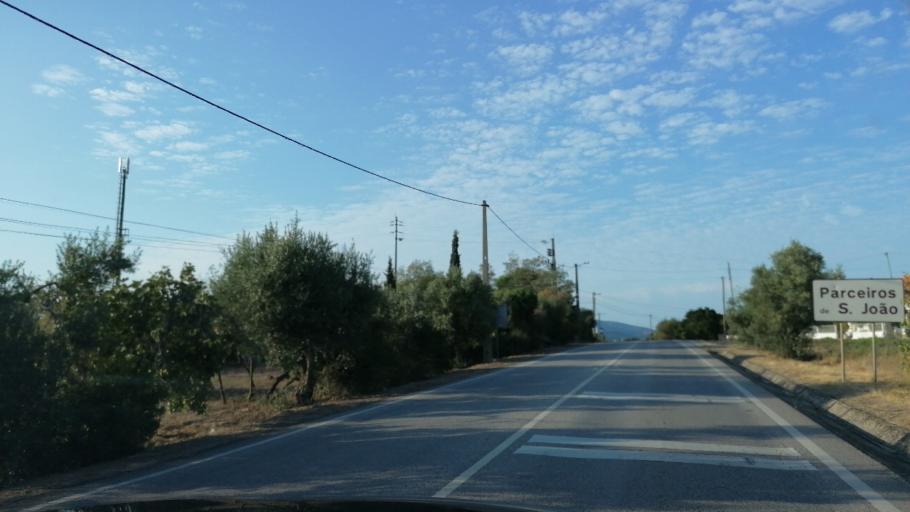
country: PT
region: Santarem
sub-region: Alcanena
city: Alcanena
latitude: 39.4450
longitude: -8.6236
